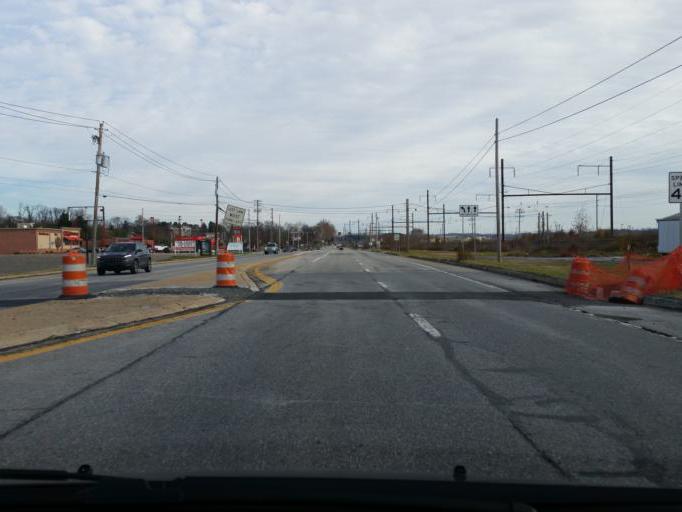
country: US
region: Pennsylvania
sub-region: Dauphin County
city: Middletown
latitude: 40.1991
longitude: -76.7584
